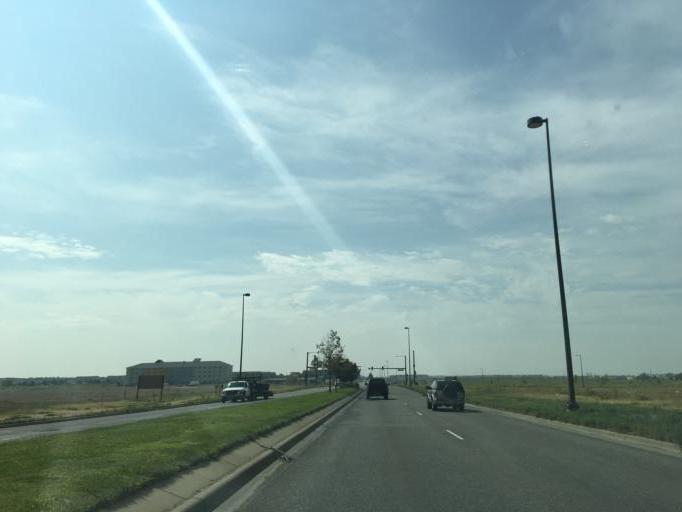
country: US
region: Colorado
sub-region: Adams County
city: Aurora
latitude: 39.8094
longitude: -104.7722
